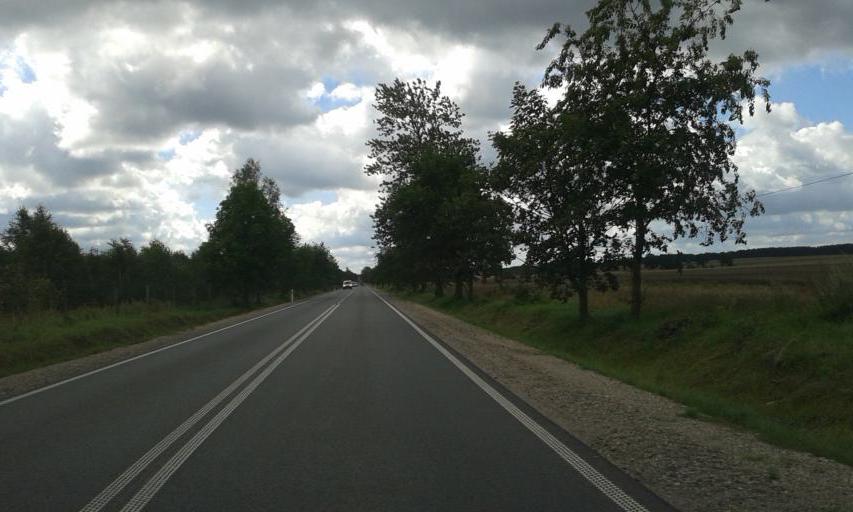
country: PL
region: West Pomeranian Voivodeship
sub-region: Powiat szczecinecki
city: Lubowo
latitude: 53.4955
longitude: 16.3342
